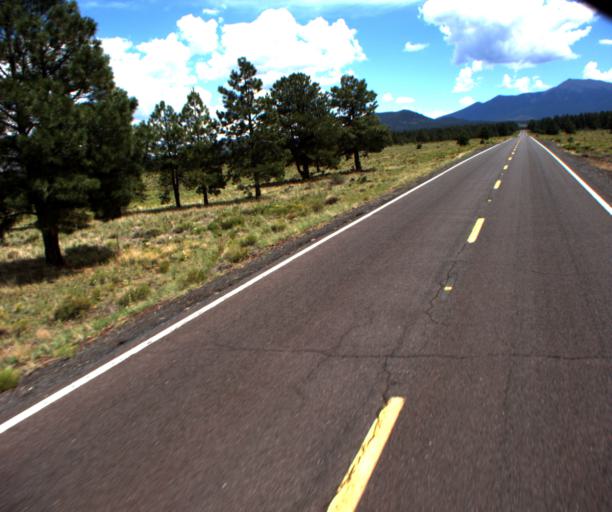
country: US
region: Arizona
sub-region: Coconino County
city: Parks
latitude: 35.4769
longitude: -111.7961
